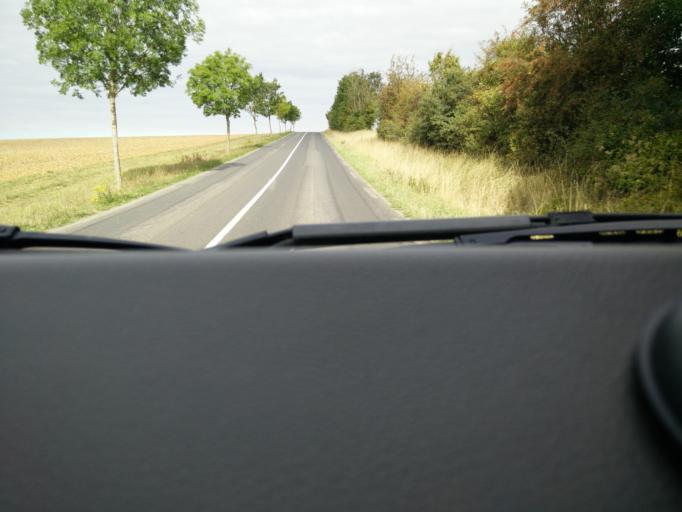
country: FR
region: Lorraine
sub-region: Departement de Meurthe-et-Moselle
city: Montauville
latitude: 48.9052
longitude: 5.9475
